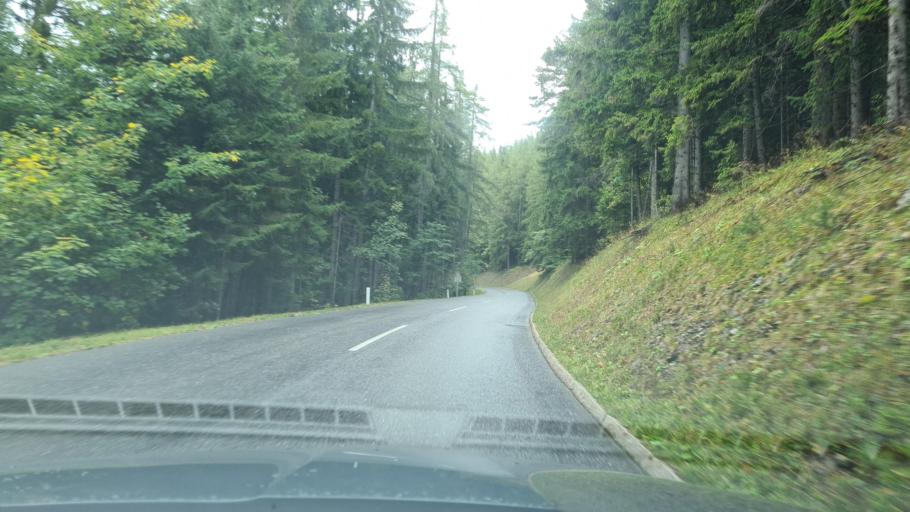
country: AT
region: Styria
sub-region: Politischer Bezirk Weiz
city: Passail
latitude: 47.3225
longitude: 15.4786
